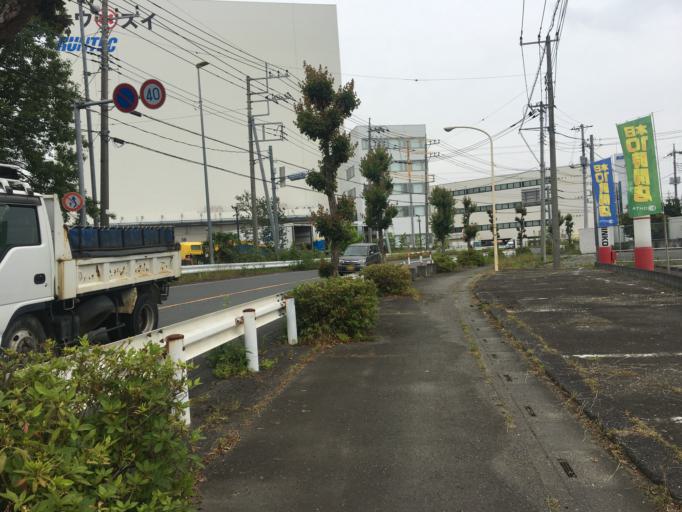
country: JP
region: Saitama
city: Sakado
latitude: 35.9946
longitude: 139.4384
